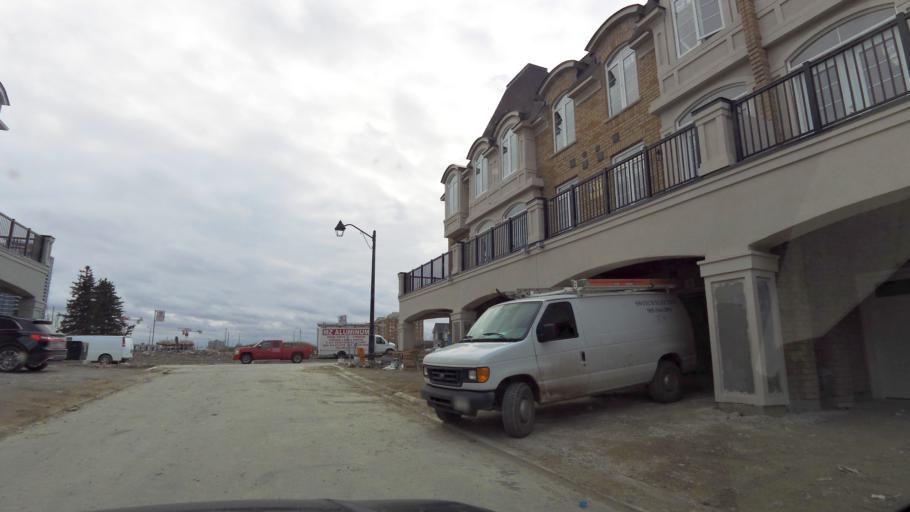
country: CA
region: Ontario
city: Mississauga
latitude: 43.6104
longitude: -79.6527
